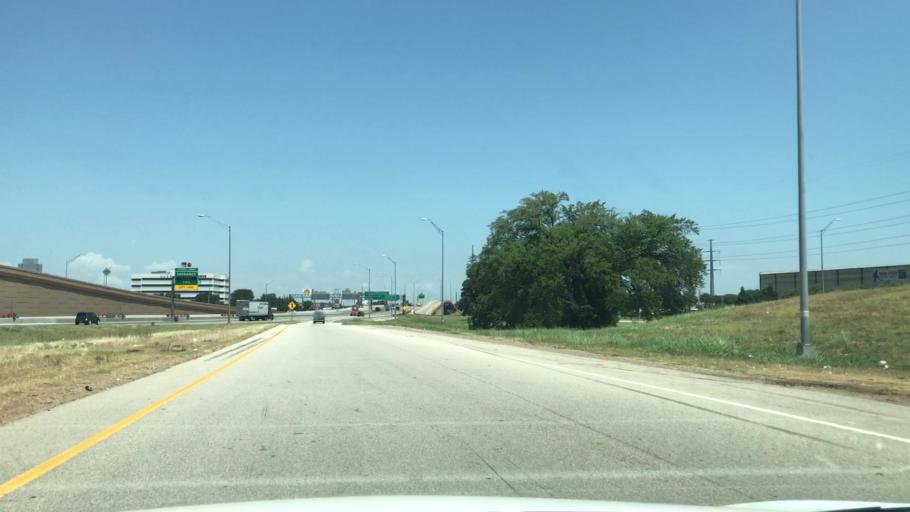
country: US
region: Texas
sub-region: Dallas County
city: Farmers Branch
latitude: 32.9177
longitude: -96.8977
